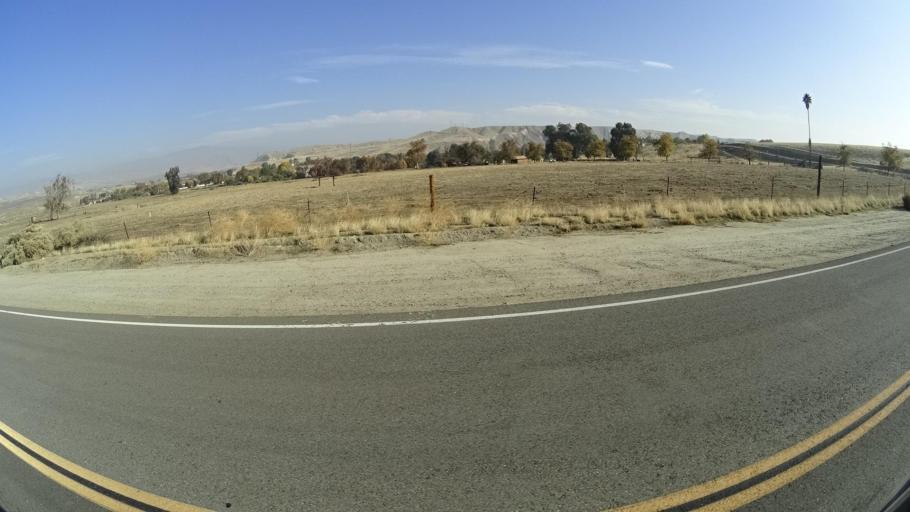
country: US
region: California
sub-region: Kern County
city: Oildale
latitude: 35.4483
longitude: -118.9465
